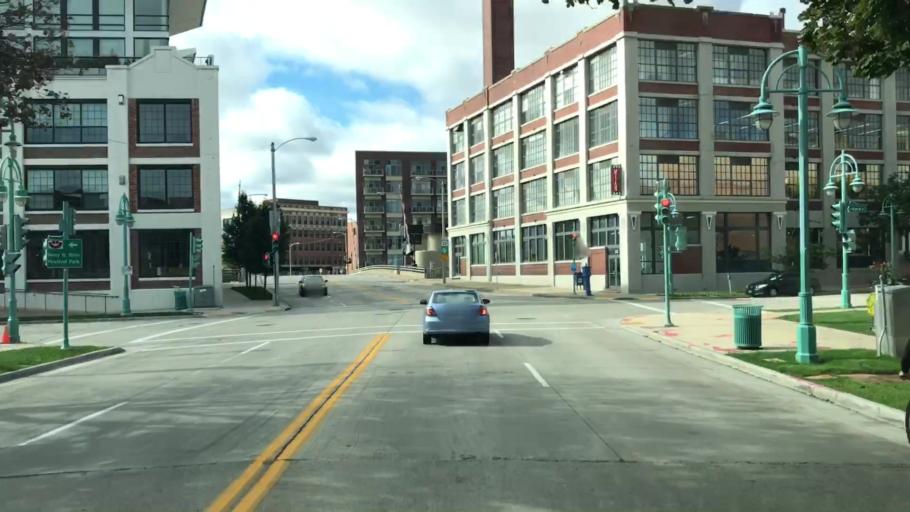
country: US
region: Wisconsin
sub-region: Milwaukee County
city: Milwaukee
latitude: 43.0310
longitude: -87.9066
